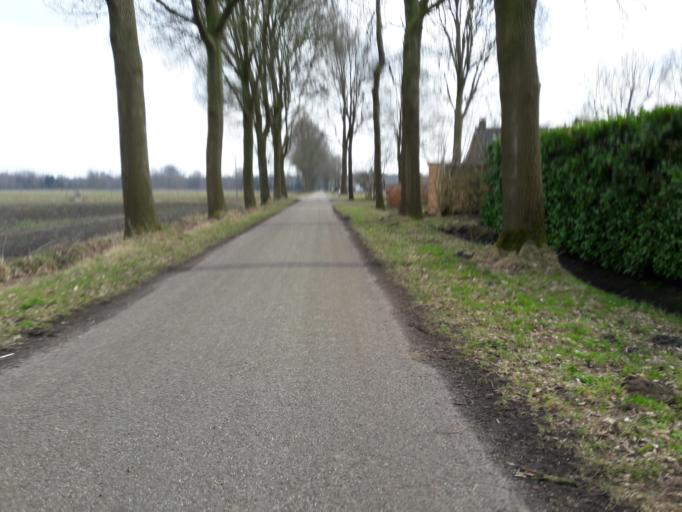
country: NL
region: Drenthe
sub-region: Gemeente Assen
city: Assen
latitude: 52.9447
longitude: 6.6487
